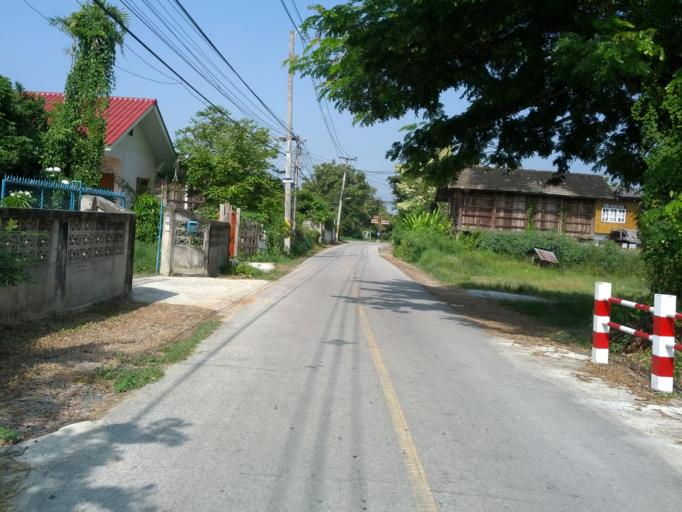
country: TH
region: Chiang Mai
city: San Sai
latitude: 18.8039
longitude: 99.0923
